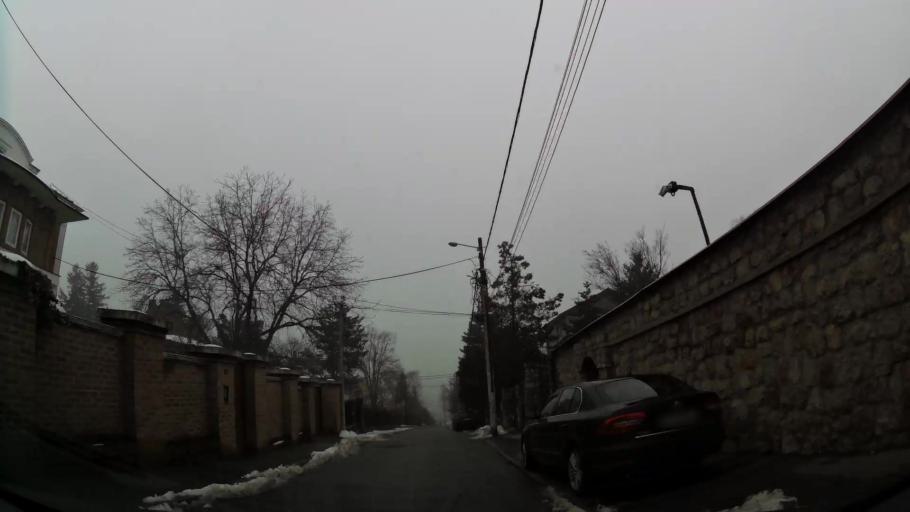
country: RS
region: Central Serbia
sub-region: Belgrade
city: Cukarica
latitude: 44.7867
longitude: 20.4359
